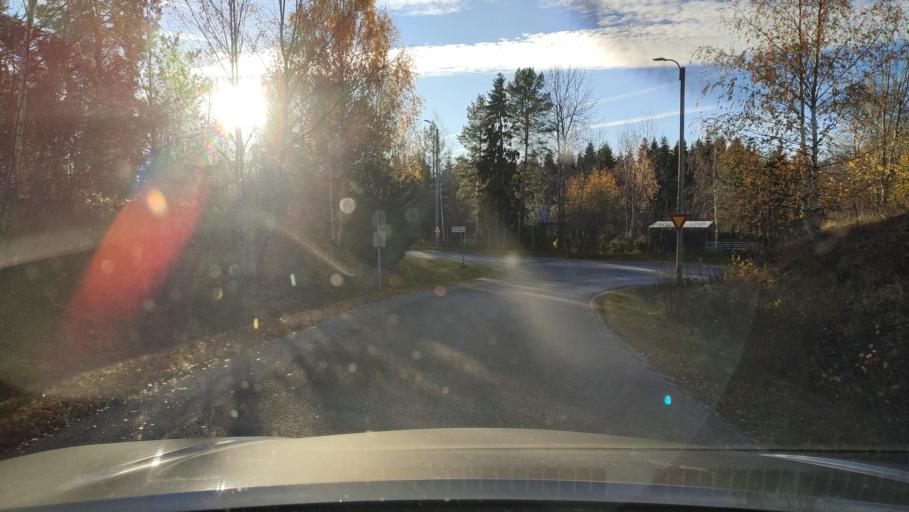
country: FI
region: Ostrobothnia
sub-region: Vaasa
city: Teeriniemi
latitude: 63.0702
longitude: 21.6907
